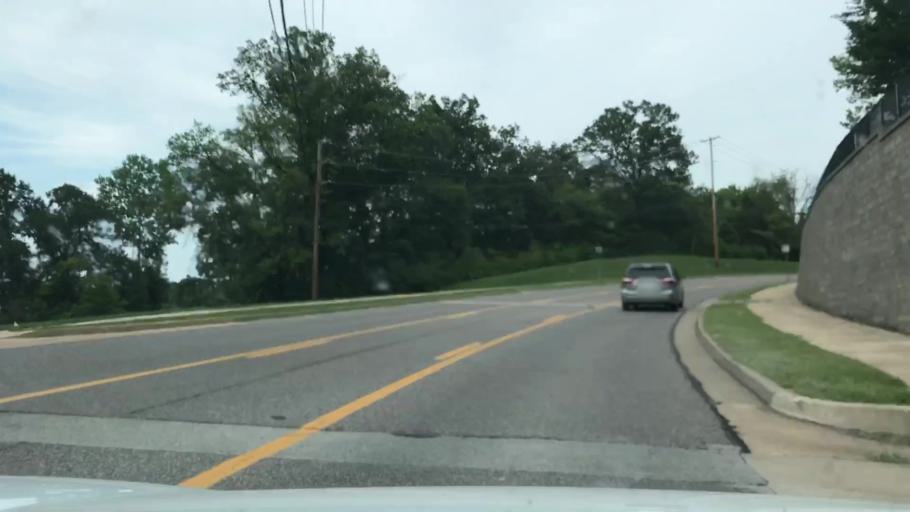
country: US
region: Missouri
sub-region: Saint Louis County
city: Clarkson Valley
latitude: 38.6238
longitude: -90.5863
